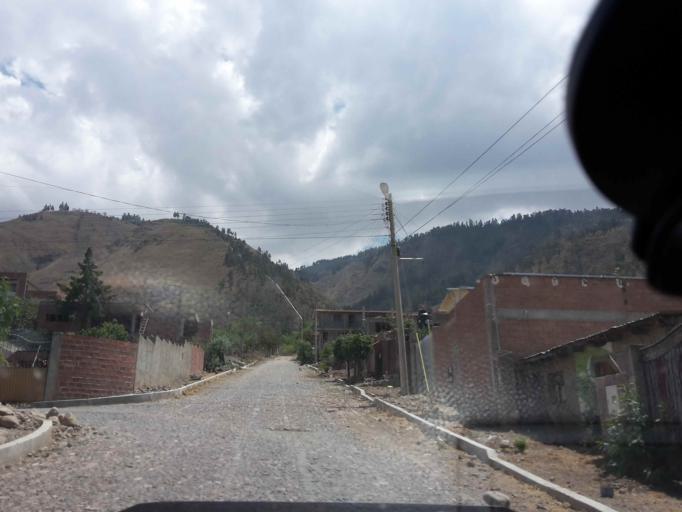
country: BO
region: Cochabamba
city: Cochabamba
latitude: -17.3215
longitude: -66.2226
